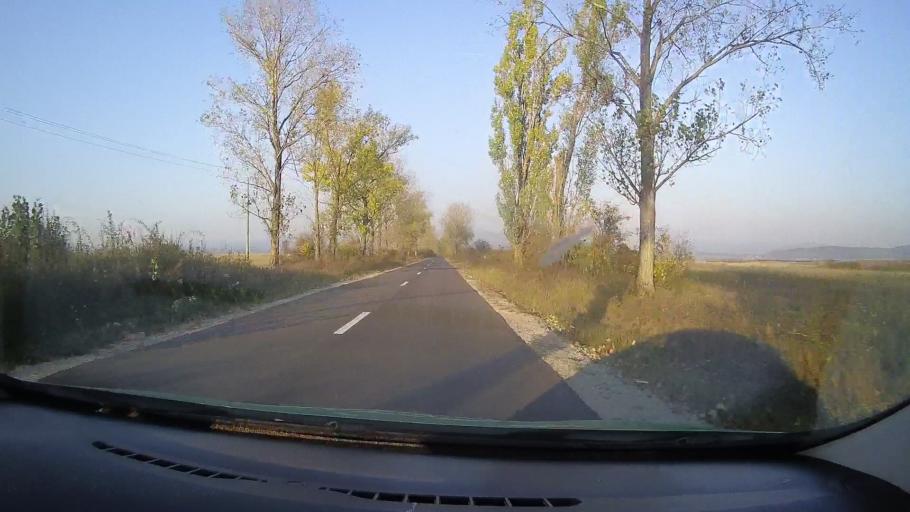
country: RO
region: Arad
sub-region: Comuna Barsa
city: Barsa
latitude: 46.3689
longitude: 22.0426
